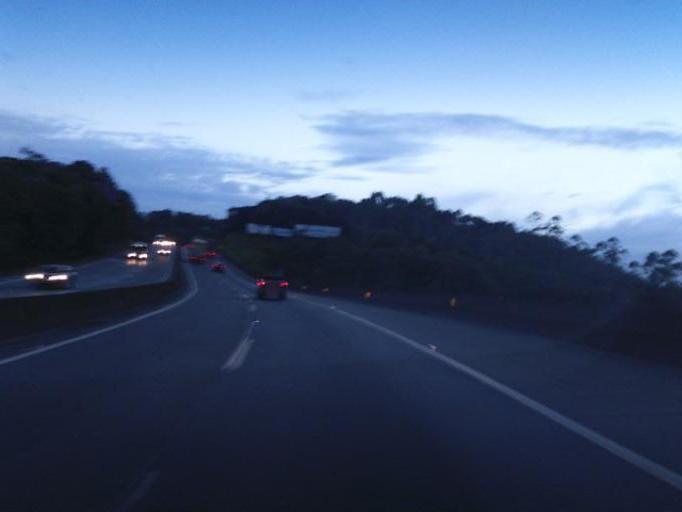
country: BR
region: Santa Catarina
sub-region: Joinville
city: Joinville
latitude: -26.3824
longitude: -48.8514
